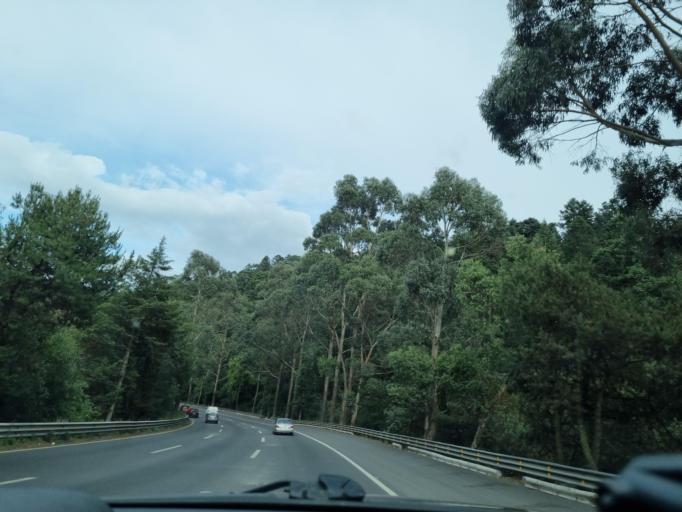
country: MX
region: Morelos
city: San Jeronimo Acazulco
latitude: 19.2920
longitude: -99.4213
